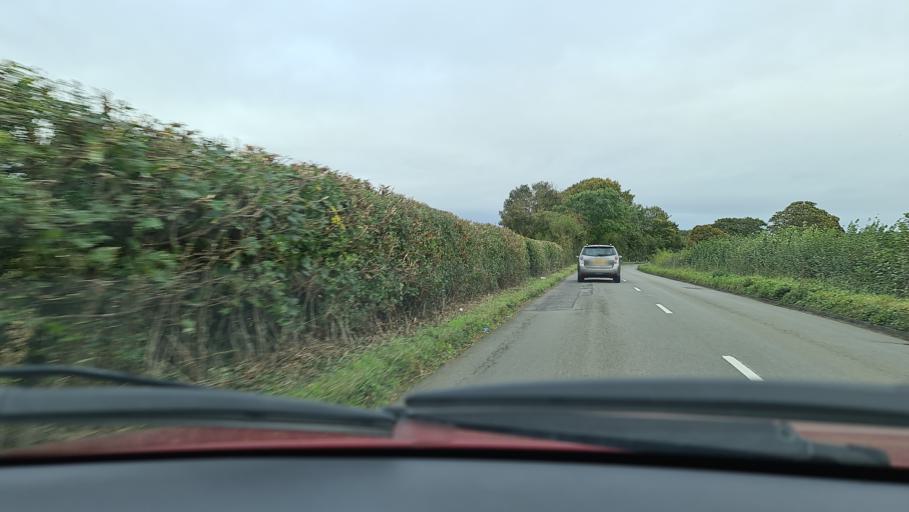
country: GB
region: England
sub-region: Oxfordshire
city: Somerton
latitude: 51.9188
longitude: -1.2396
